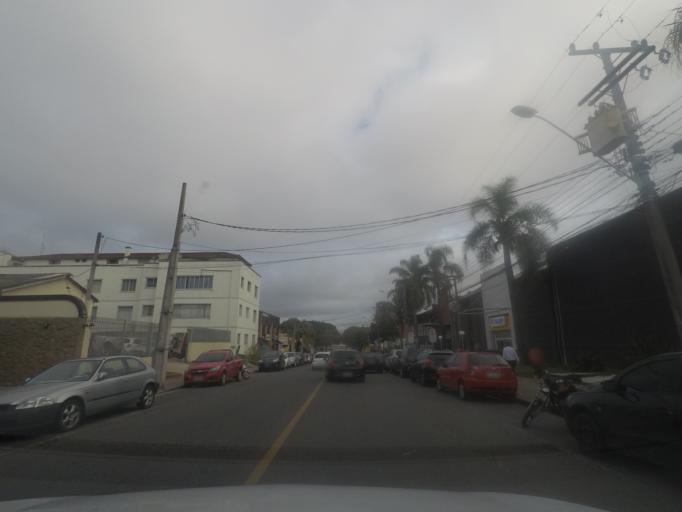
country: BR
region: Parana
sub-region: Curitiba
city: Curitiba
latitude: -25.4253
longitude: -49.2474
